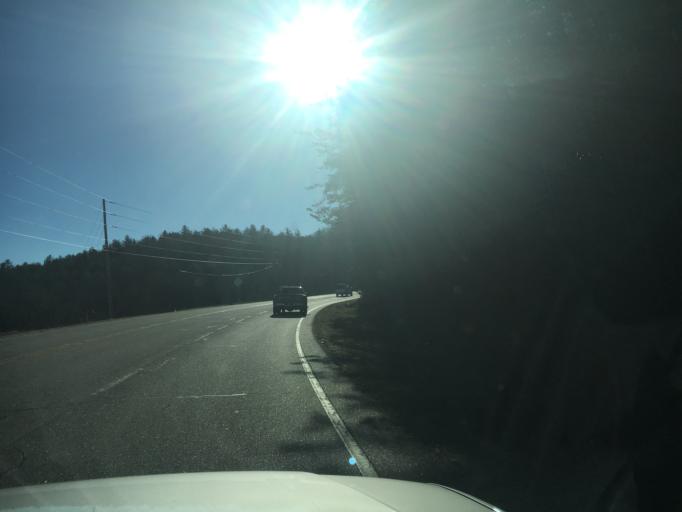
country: US
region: Georgia
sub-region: Union County
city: Blairsville
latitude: 34.7931
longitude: -83.8944
